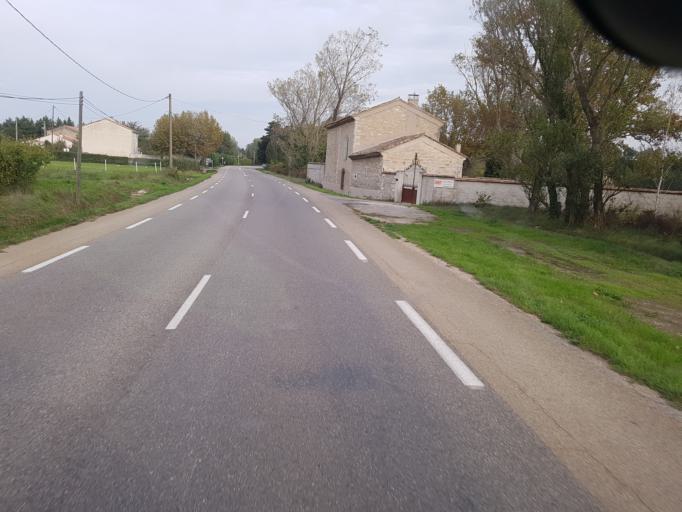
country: FR
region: Provence-Alpes-Cote d'Azur
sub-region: Departement des Bouches-du-Rhone
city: Rognonas
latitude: 43.9085
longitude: 4.7849
